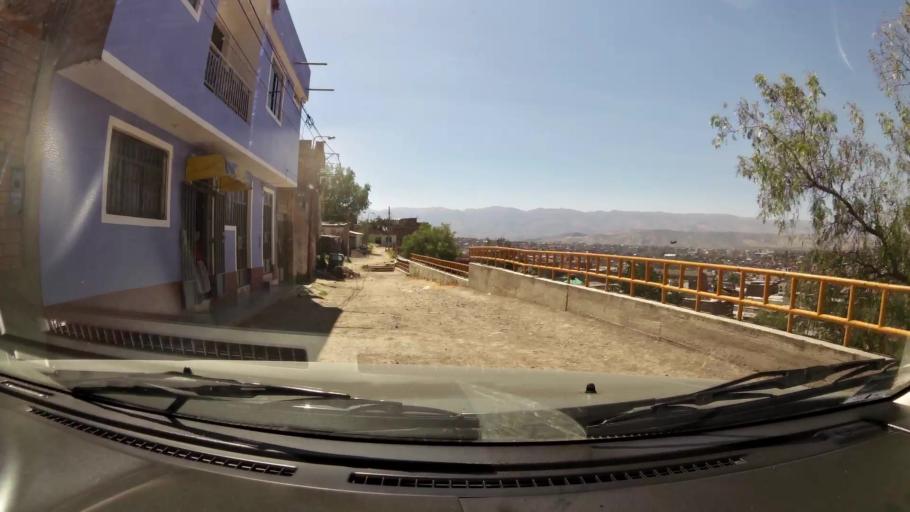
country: PE
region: Ayacucho
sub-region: Provincia de Huamanga
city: Ayacucho
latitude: -13.1655
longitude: -74.2307
